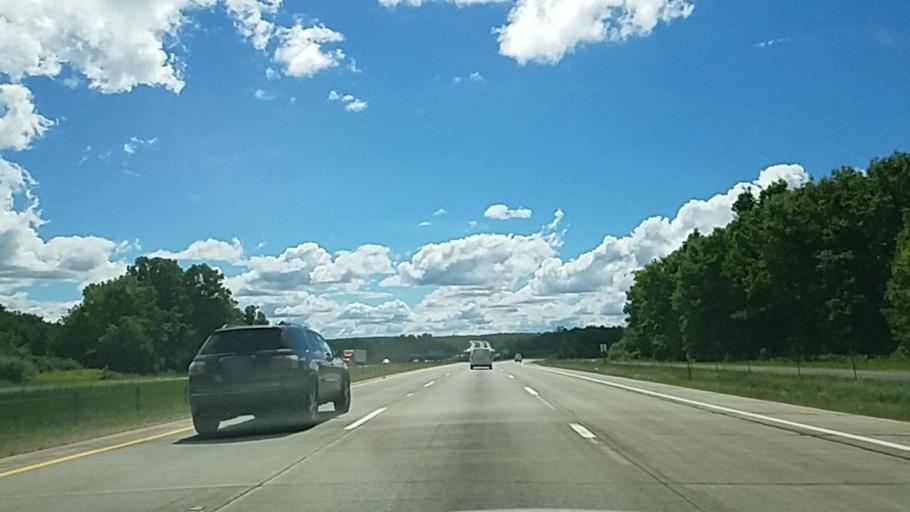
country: US
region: Michigan
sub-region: Genesee County
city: Fenton
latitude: 42.7731
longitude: -83.7497
